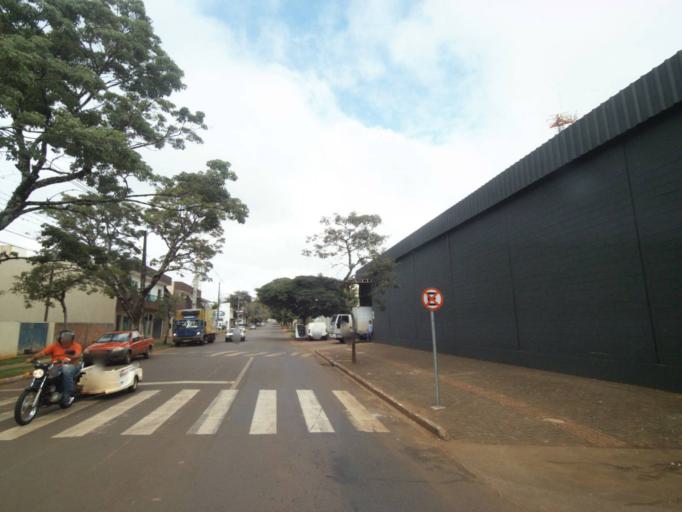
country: BR
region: Parana
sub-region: Campo Mourao
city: Campo Mourao
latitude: -24.0282
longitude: -52.3637
